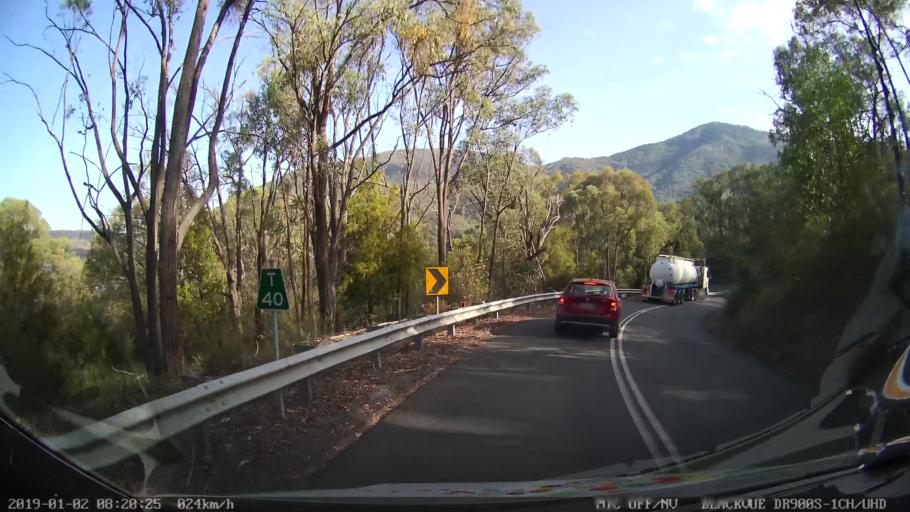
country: AU
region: New South Wales
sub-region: Tumut Shire
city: Tumut
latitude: -35.5725
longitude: 148.3239
